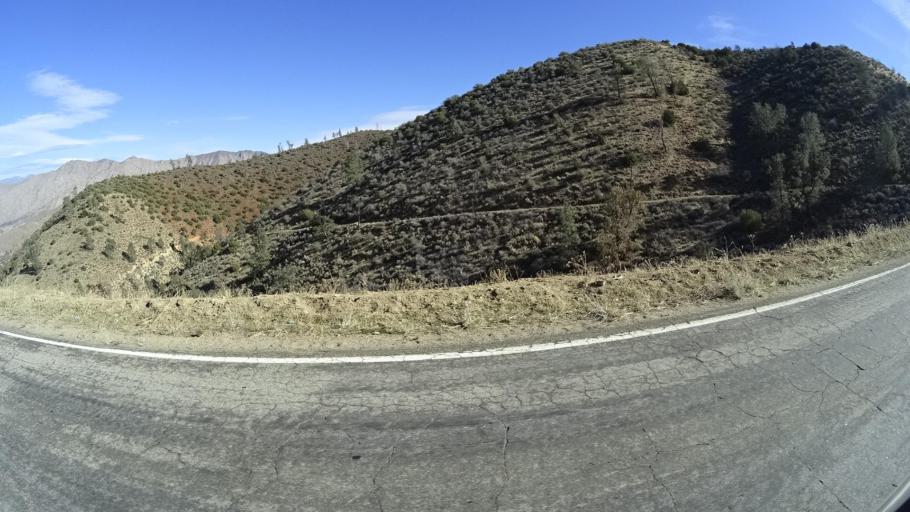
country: US
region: California
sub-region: Kern County
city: Bodfish
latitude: 35.5716
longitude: -118.5070
